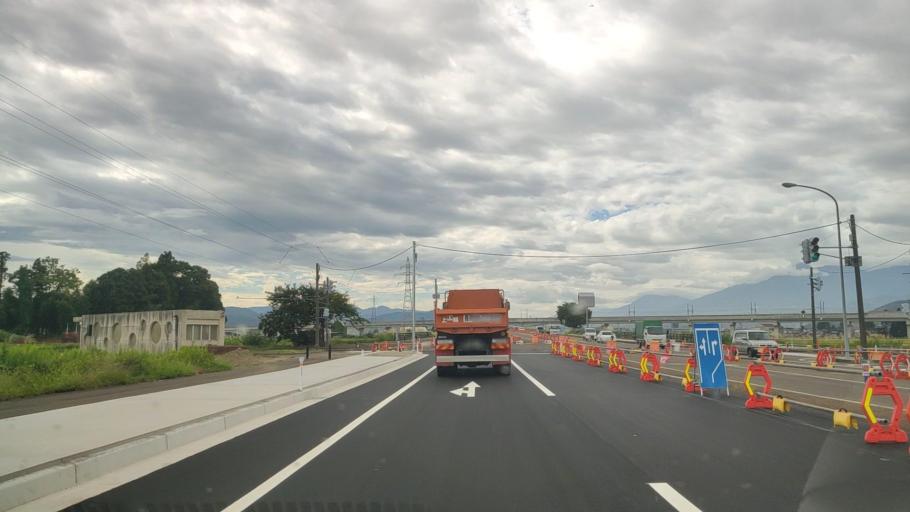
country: JP
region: Niigata
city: Joetsu
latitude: 37.0732
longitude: 138.2648
